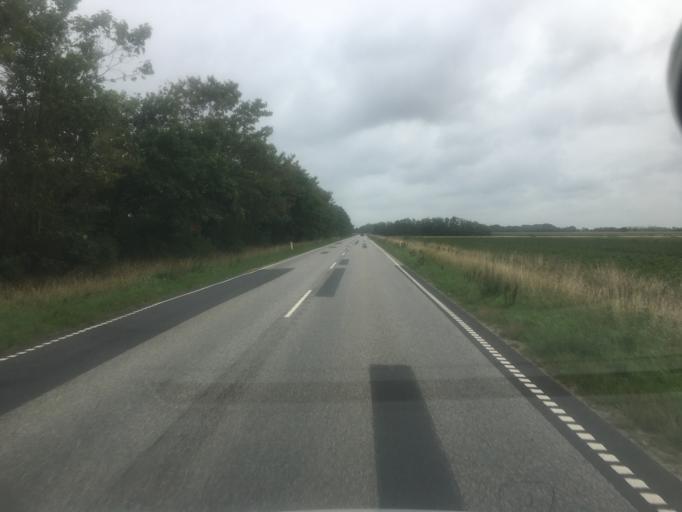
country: DK
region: South Denmark
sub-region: Tonder Kommune
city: Logumkloster
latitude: 54.9720
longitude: 8.9688
